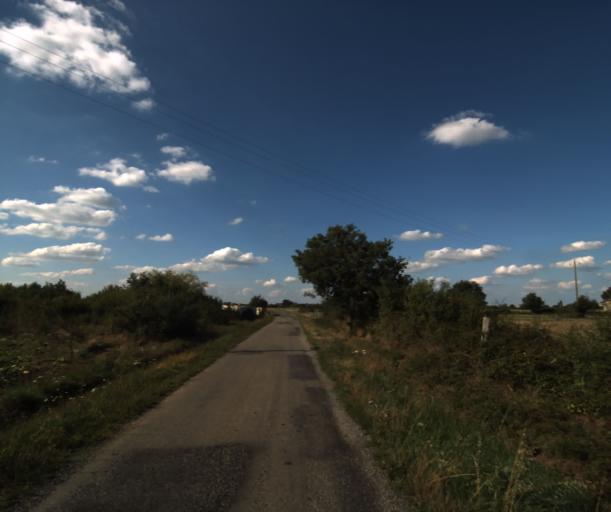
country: FR
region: Midi-Pyrenees
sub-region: Departement de la Haute-Garonne
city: Saint-Lys
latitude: 43.4940
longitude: 1.1946
